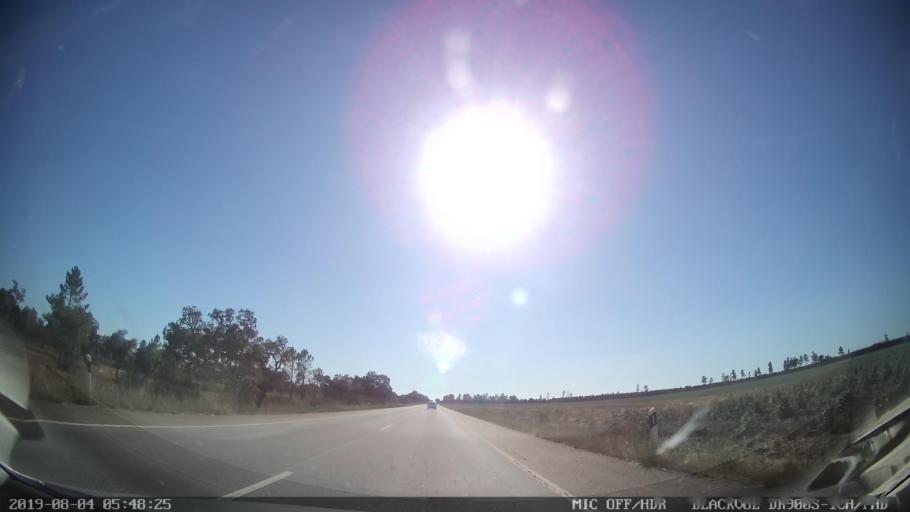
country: PT
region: Portalegre
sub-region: Gaviao
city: Gaviao
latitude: 39.4451
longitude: -7.8254
